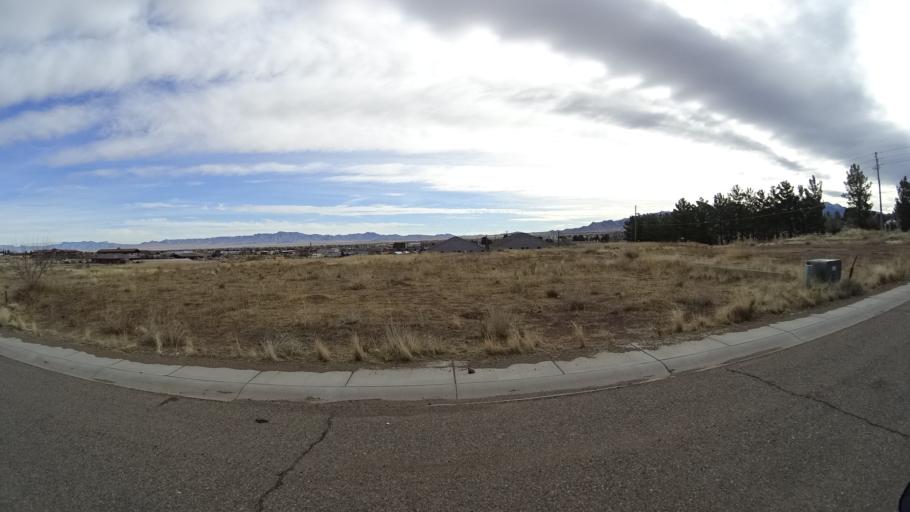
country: US
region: Arizona
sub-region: Mohave County
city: Kingman
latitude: 35.2226
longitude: -114.0465
